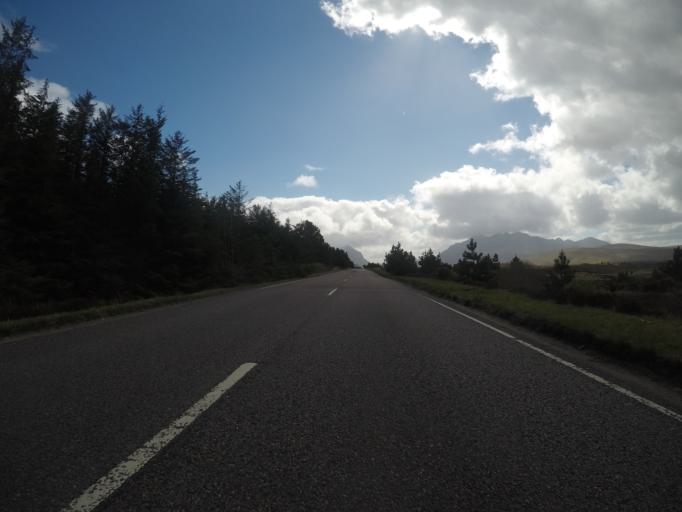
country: GB
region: Scotland
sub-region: Highland
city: Isle of Skye
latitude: 57.3177
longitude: -6.2023
